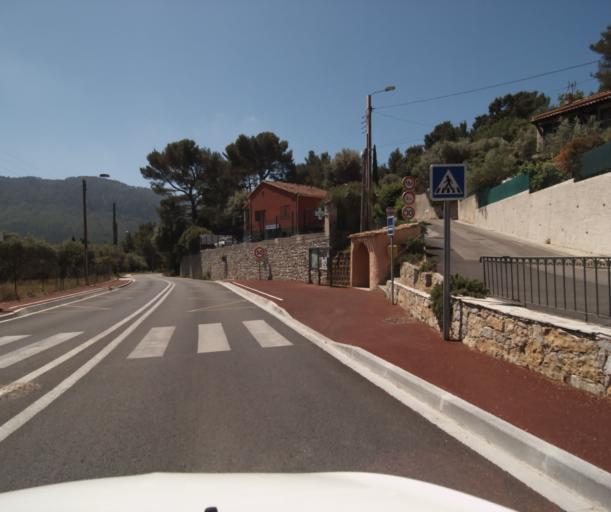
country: FR
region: Provence-Alpes-Cote d'Azur
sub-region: Departement du Var
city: Le Revest-les-Eaux
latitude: 43.1706
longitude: 5.9205
